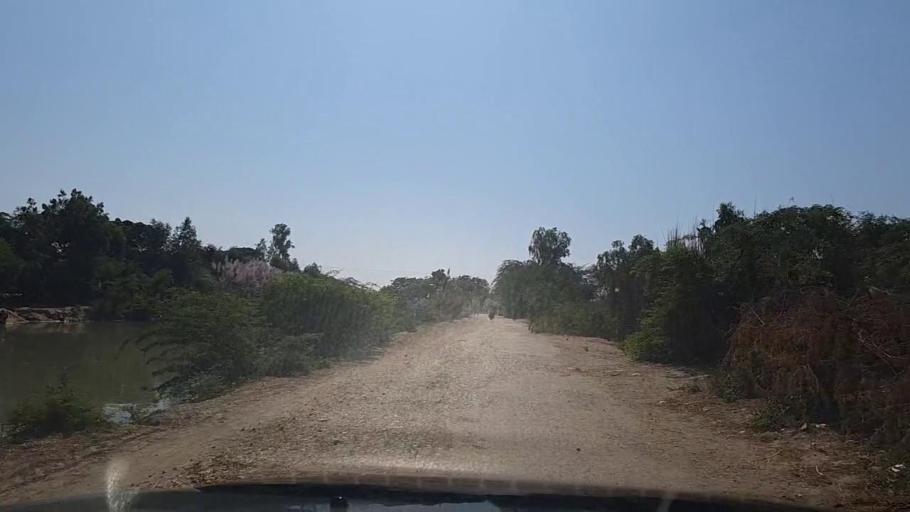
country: PK
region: Sindh
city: Thatta
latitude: 24.5973
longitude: 67.8198
